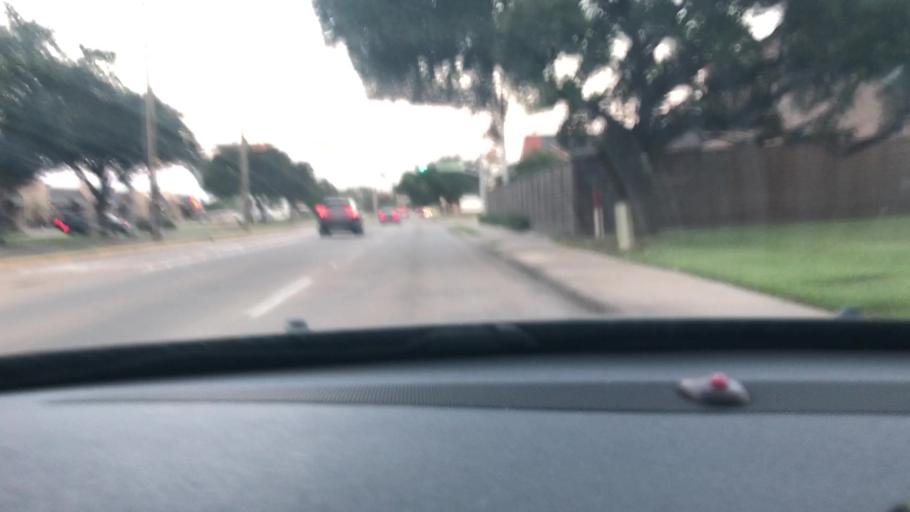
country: US
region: Texas
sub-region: Harris County
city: Webster
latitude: 29.5517
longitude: -95.1151
